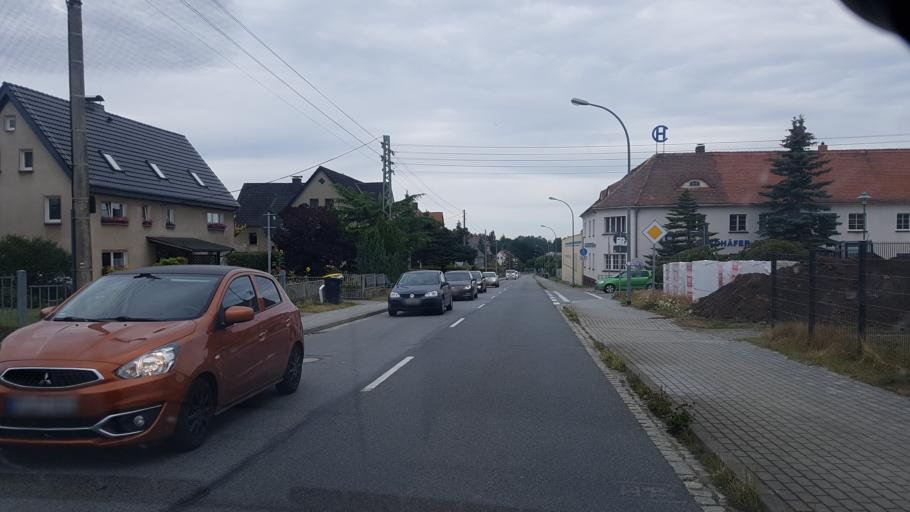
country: DE
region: Saxony
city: Ohorn
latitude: 51.1704
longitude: 14.0438
